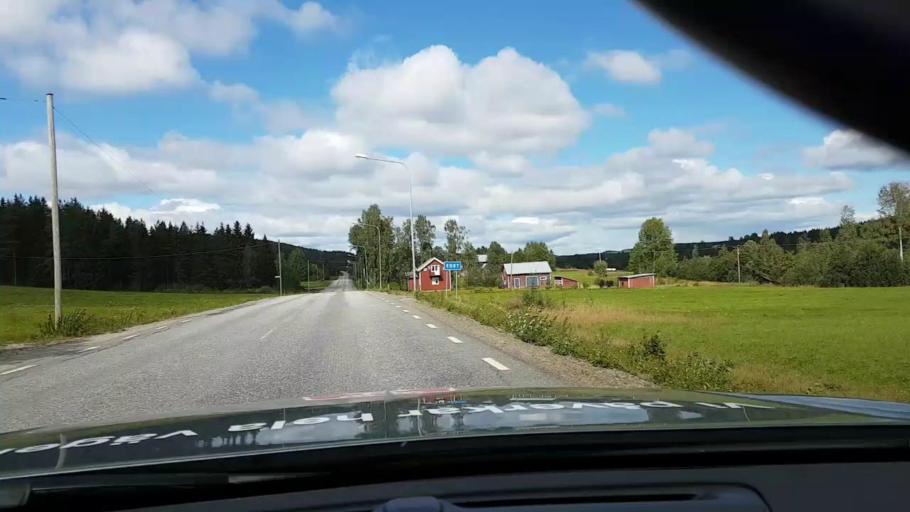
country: SE
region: Vaesternorrland
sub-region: OErnskoeldsviks Kommun
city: Bredbyn
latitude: 63.4797
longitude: 18.0922
